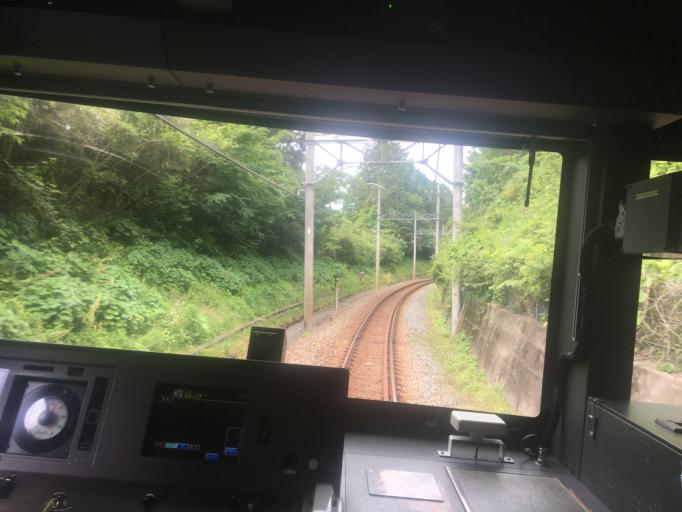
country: JP
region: Saitama
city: Ogawa
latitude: 36.0515
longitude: 139.2896
